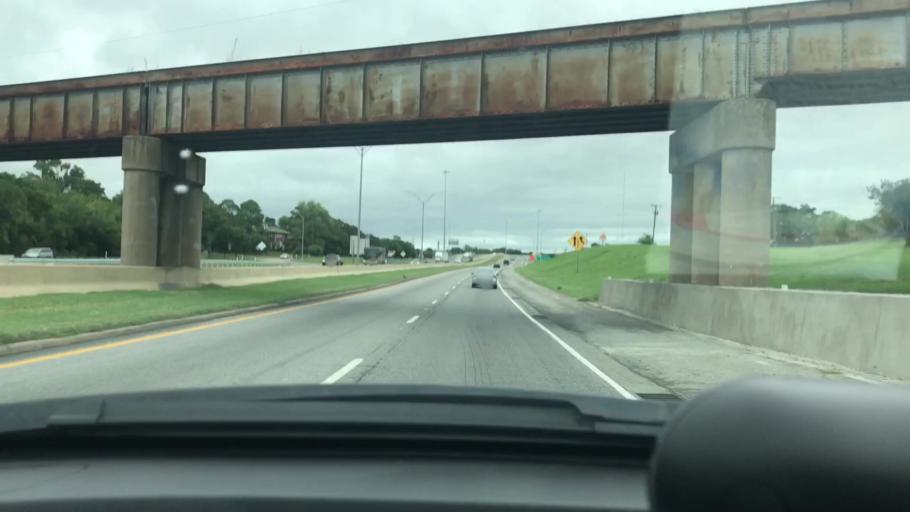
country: US
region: Texas
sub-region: Grayson County
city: Sherman
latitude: 33.6422
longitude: -96.6150
